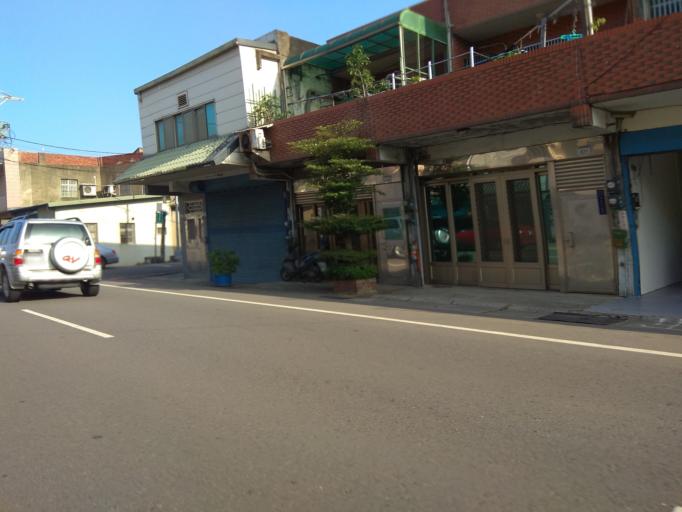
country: TW
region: Taiwan
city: Taoyuan City
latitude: 24.9633
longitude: 121.1434
